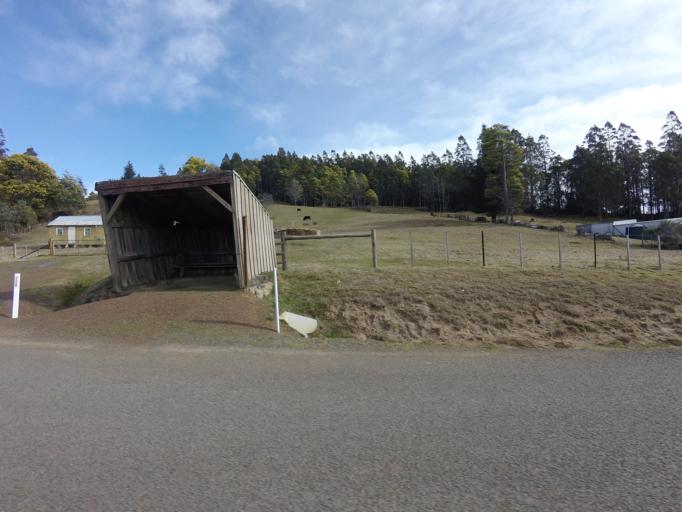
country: AU
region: Tasmania
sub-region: Kingborough
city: Margate
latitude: -43.0200
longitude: 147.1645
